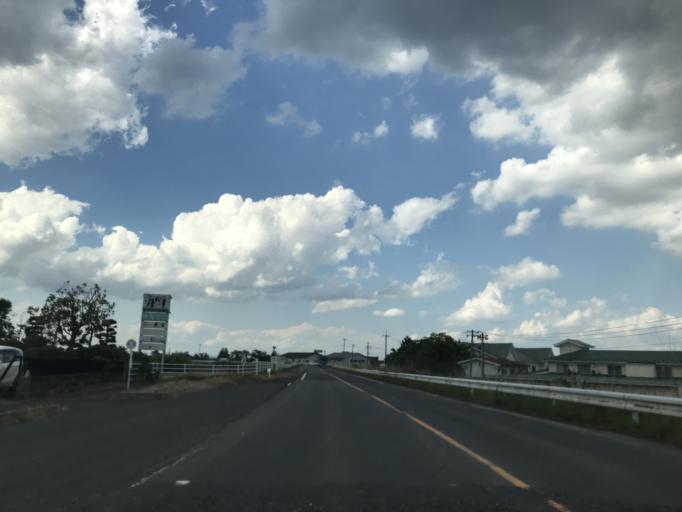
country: JP
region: Miyagi
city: Wakuya
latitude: 38.6483
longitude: 141.2172
